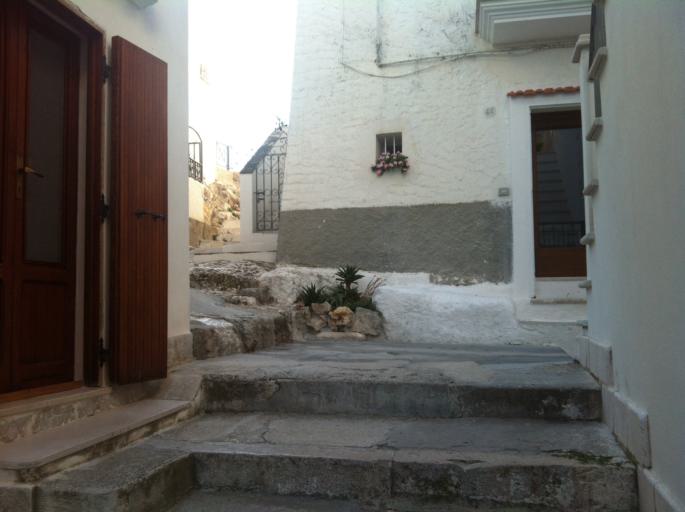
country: IT
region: Apulia
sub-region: Provincia di Foggia
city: Vieste
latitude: 41.8809
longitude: 16.1804
